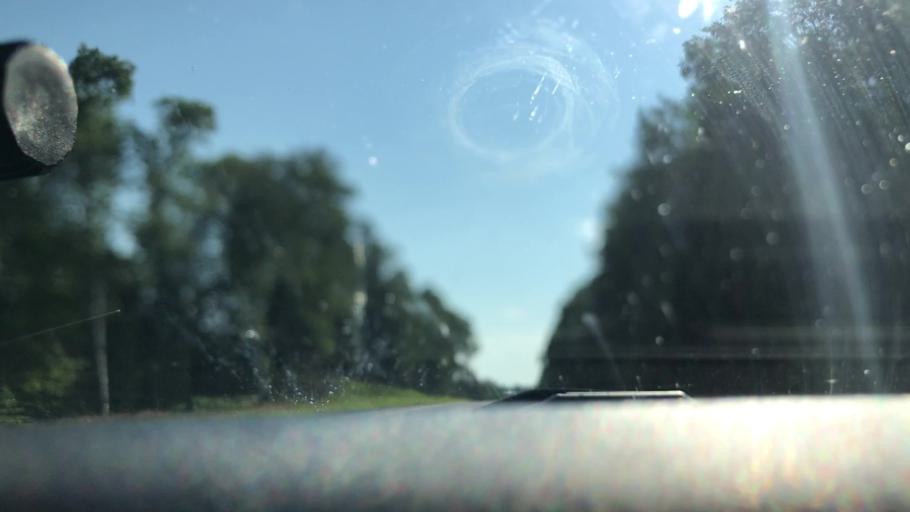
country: US
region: Minnesota
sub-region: Cook County
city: Grand Marais
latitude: 47.8203
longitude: -90.0421
